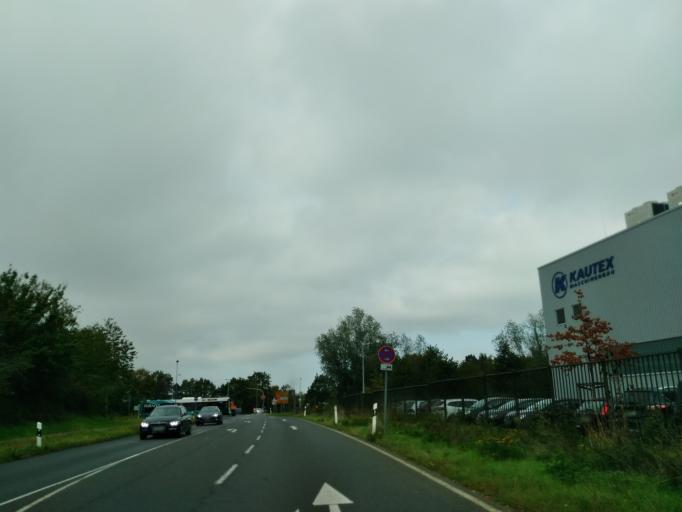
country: DE
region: North Rhine-Westphalia
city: Sankt Augustin
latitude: 50.7517
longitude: 7.1584
